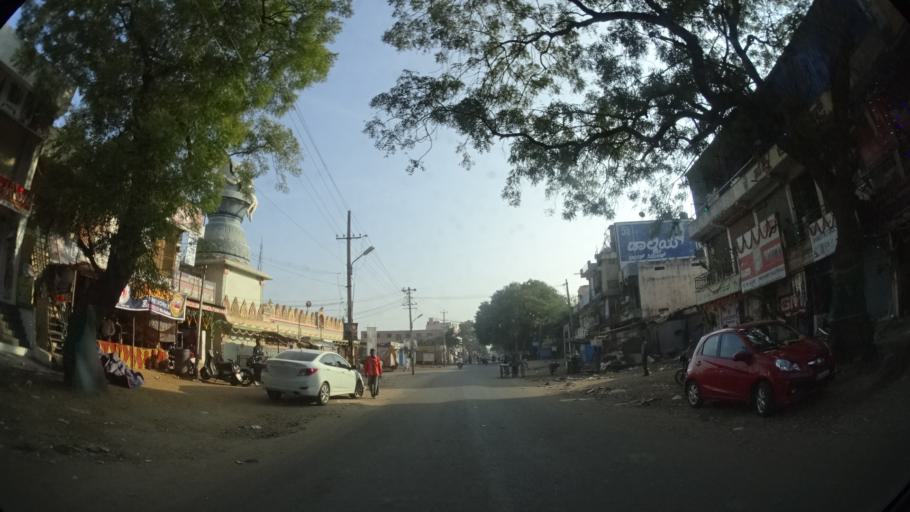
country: IN
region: Karnataka
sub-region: Bellary
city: Hospet
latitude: 15.2654
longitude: 76.3860
